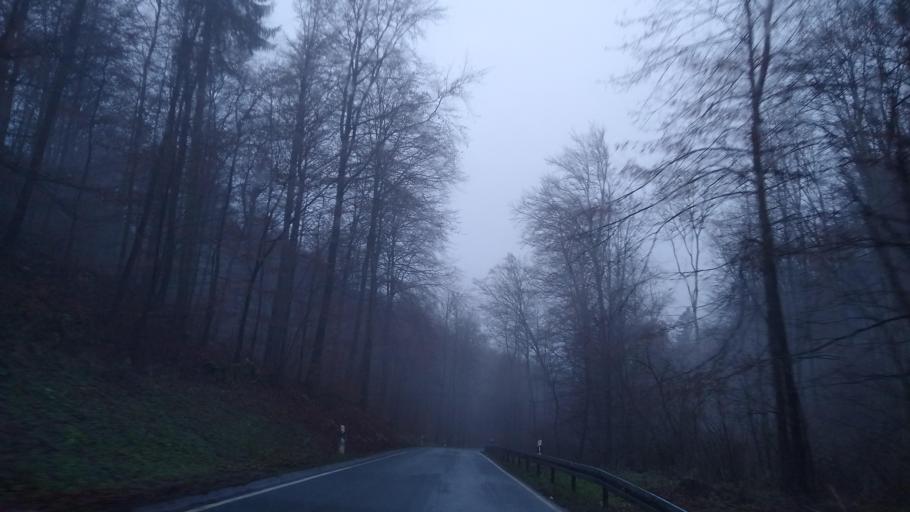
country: DE
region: Lower Saxony
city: Ottenstein
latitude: 51.9385
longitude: 9.3845
